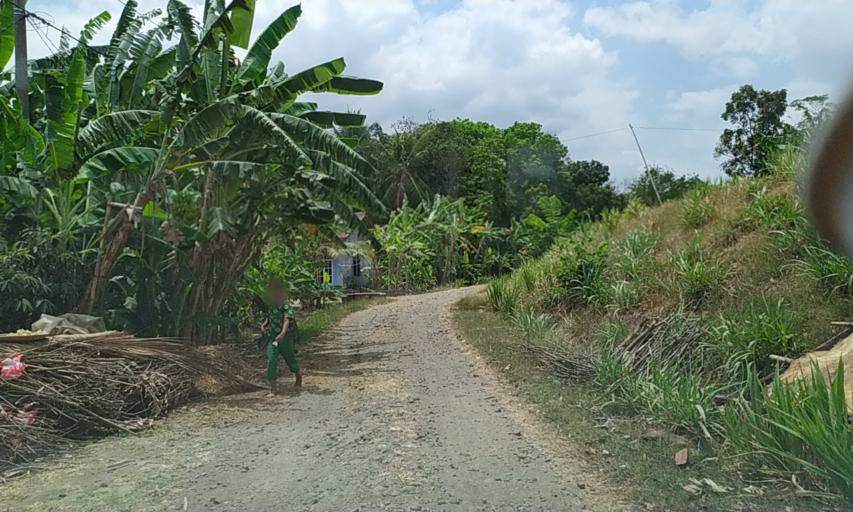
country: ID
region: Central Java
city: Winangun
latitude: -7.3657
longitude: 108.6924
